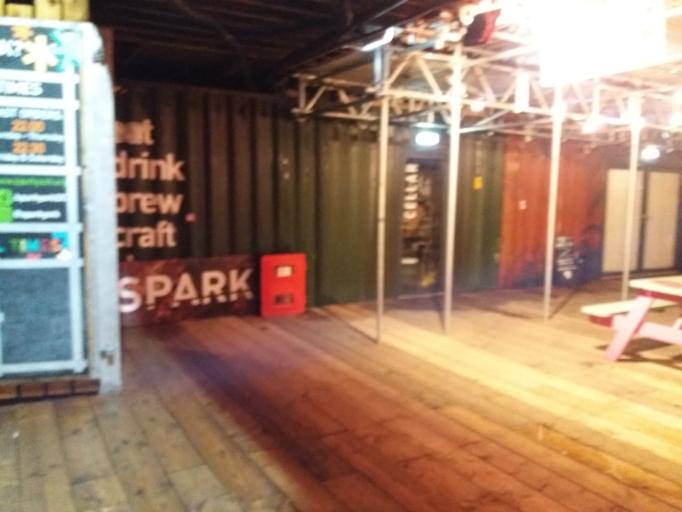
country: GB
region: England
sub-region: City of York
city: York
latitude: 53.9572
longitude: -1.0779
